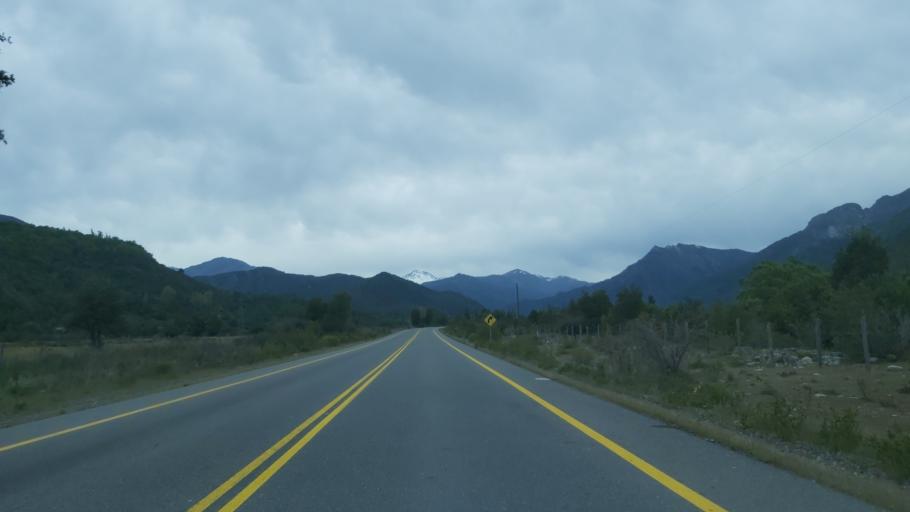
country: CL
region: Maule
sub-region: Provincia de Linares
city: Colbun
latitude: -35.7394
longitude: -71.0101
